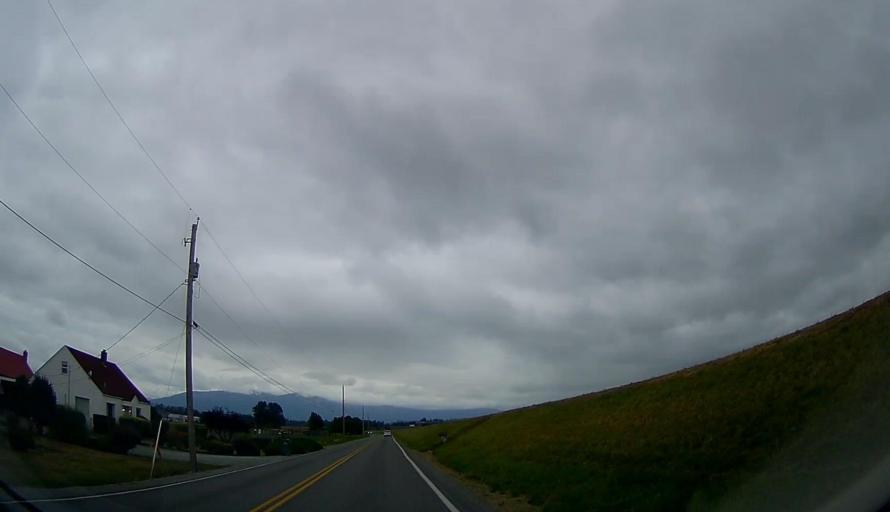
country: US
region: Washington
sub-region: Skagit County
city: Mount Vernon
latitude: 48.4471
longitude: -122.3519
